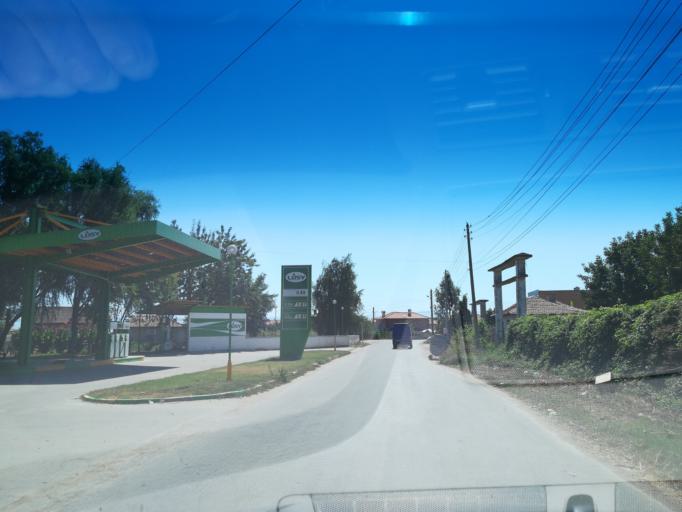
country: BG
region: Pazardzhik
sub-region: Obshtina Pazardzhik
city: Pazardzhik
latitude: 42.2725
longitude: 24.3967
